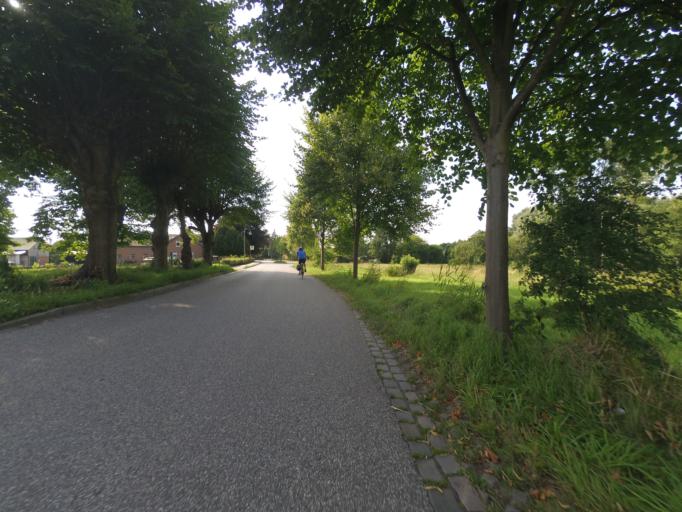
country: DE
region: Schleswig-Holstein
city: Oststeinbek
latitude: 53.5061
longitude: 10.1652
